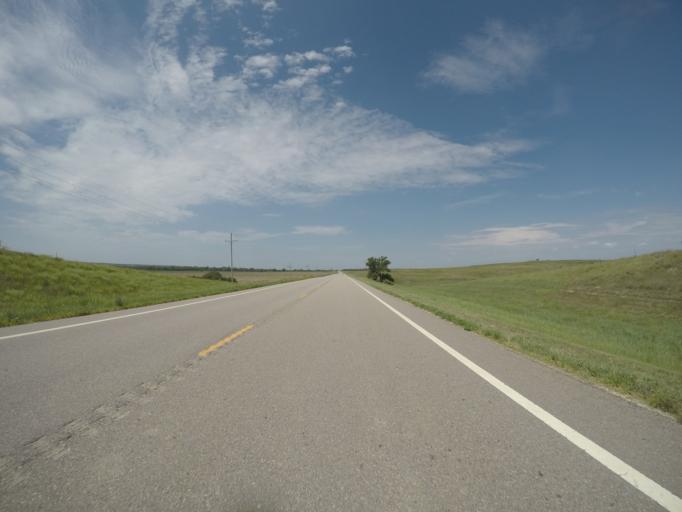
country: US
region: Kansas
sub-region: Rooks County
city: Stockton
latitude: 39.4445
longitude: -99.1686
